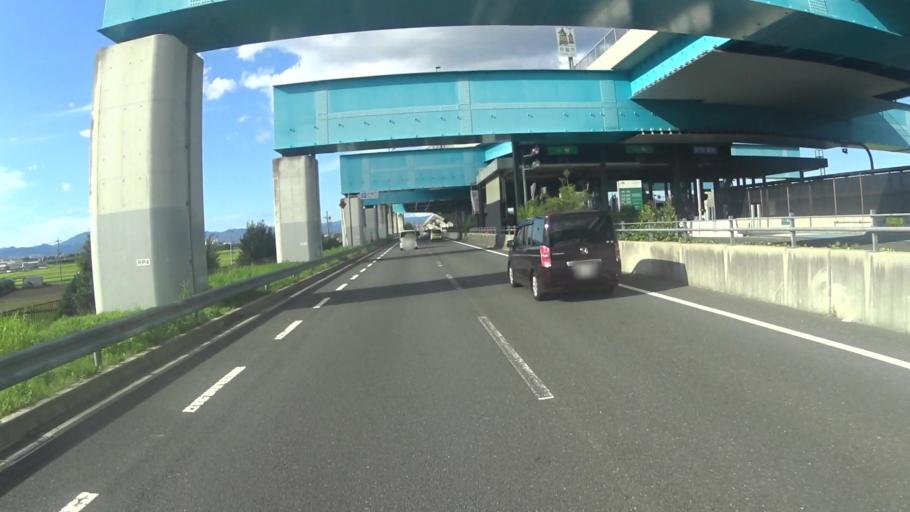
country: JP
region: Kyoto
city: Uji
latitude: 34.9076
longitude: 135.7493
